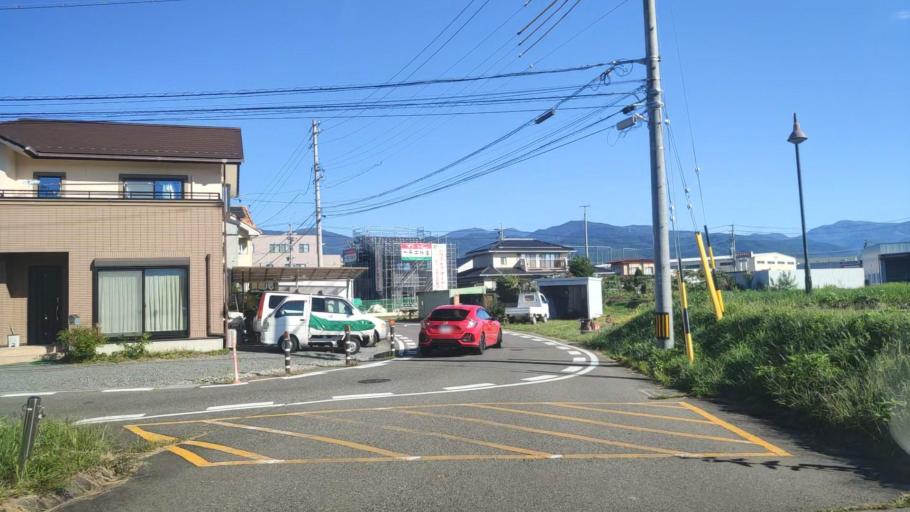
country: JP
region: Nagano
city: Okaya
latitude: 36.0594
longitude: 138.0647
